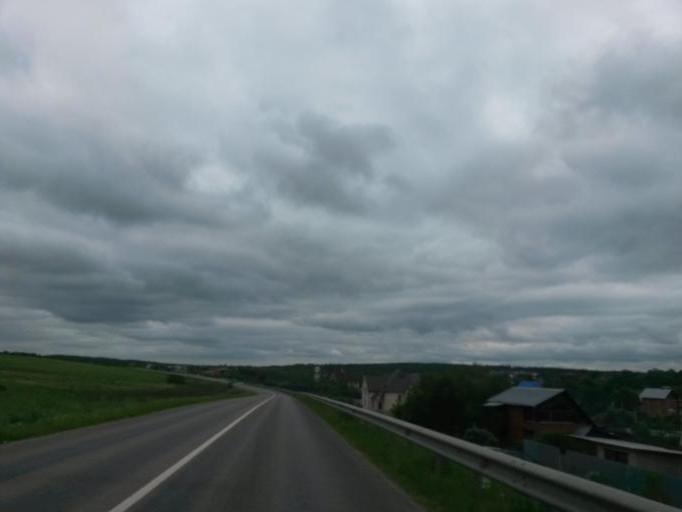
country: RU
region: Moskovskaya
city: Lyubuchany
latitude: 55.2951
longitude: 37.6322
